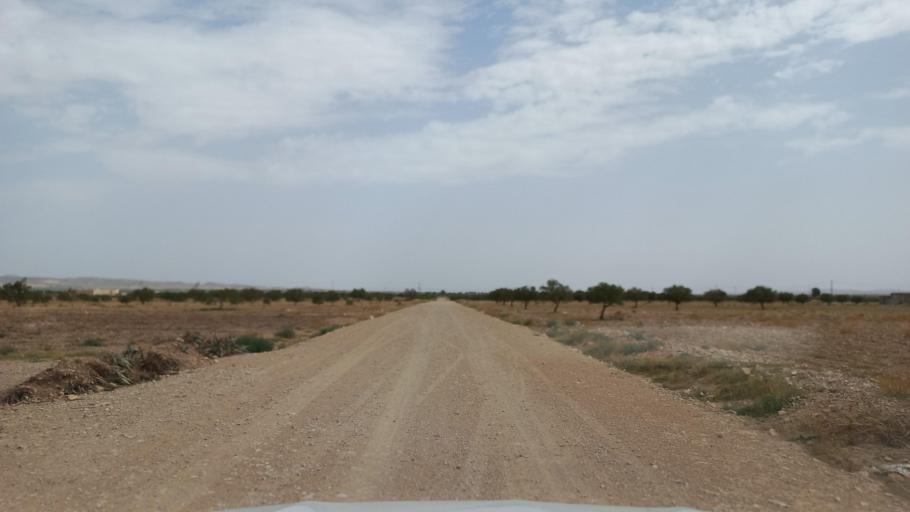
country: TN
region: Al Qasrayn
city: Kasserine
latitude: 35.2794
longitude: 9.0146
